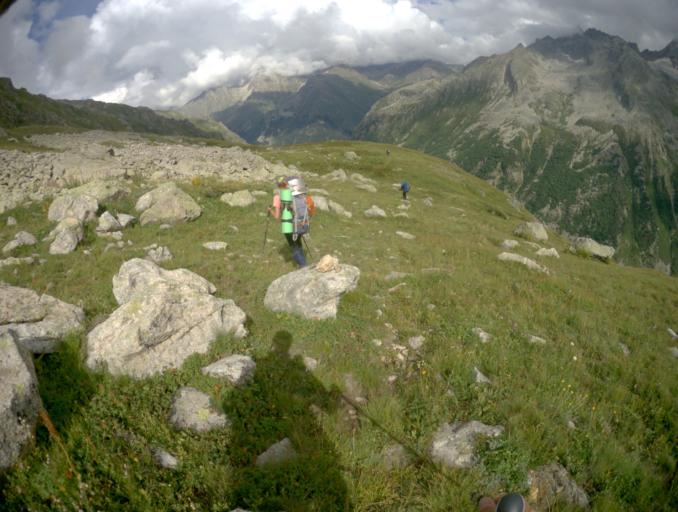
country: RU
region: Karachayevo-Cherkesiya
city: Uchkulan
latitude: 43.2678
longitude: 42.1292
